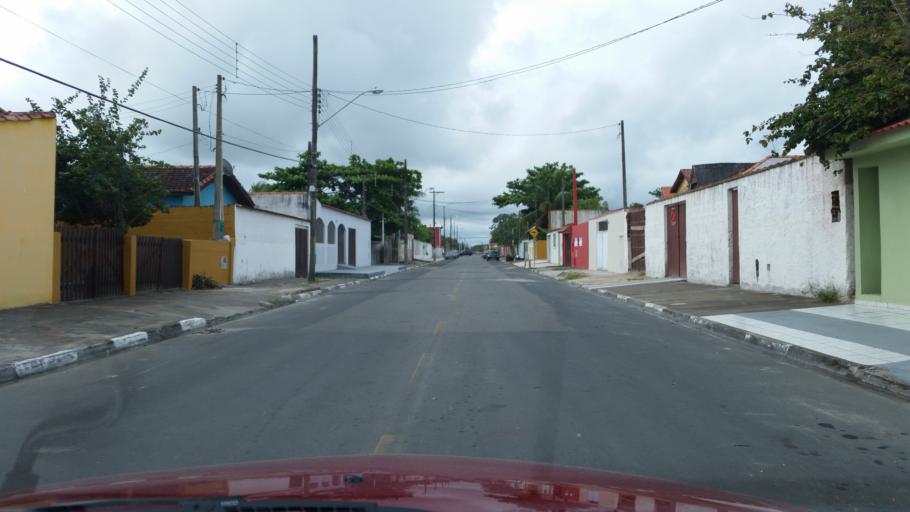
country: BR
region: Sao Paulo
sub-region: Iguape
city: Iguape
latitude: -24.7491
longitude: -47.5533
